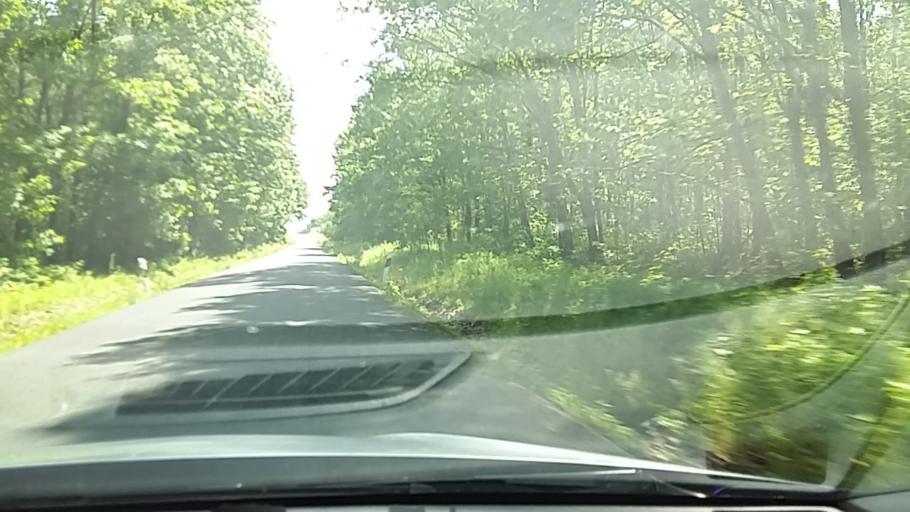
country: HU
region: Vas
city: Kormend
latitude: 46.9660
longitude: 16.5867
